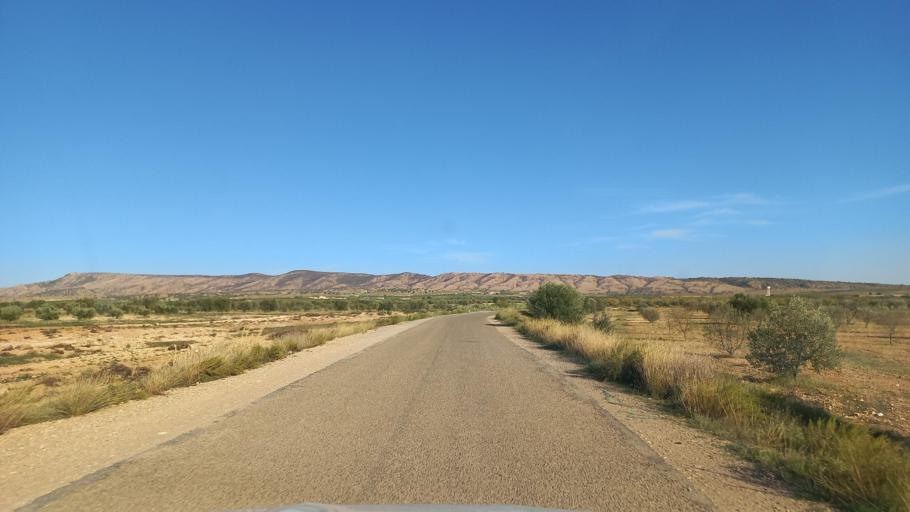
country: TN
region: Al Qasrayn
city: Sbiba
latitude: 35.3350
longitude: 9.0996
